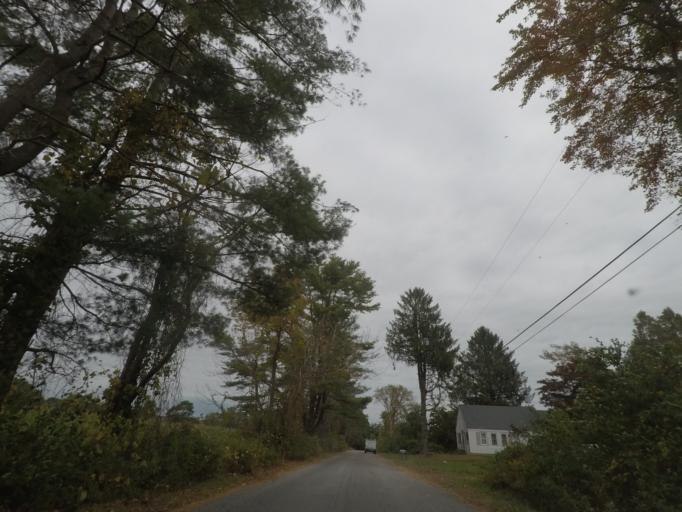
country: US
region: Connecticut
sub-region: Windham County
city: Thompson
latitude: 41.9525
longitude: -71.8337
